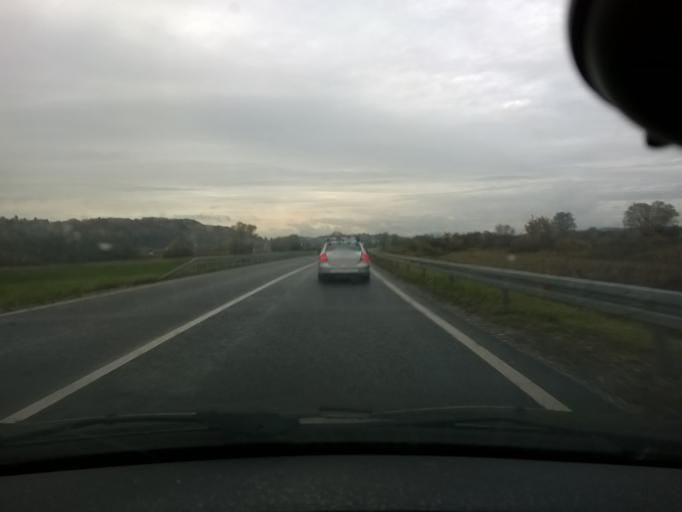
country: HR
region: Zagrebacka
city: Jakovlje
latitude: 45.9824
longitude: 15.8456
